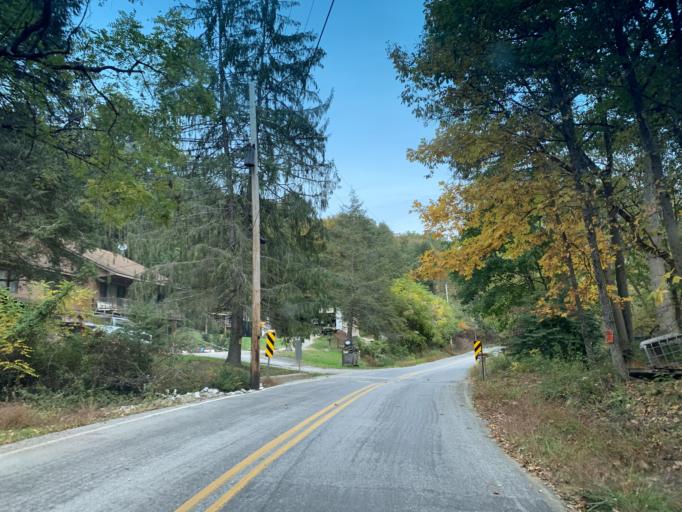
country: US
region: Pennsylvania
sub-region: York County
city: Windsor
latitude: 39.8359
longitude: -76.5173
